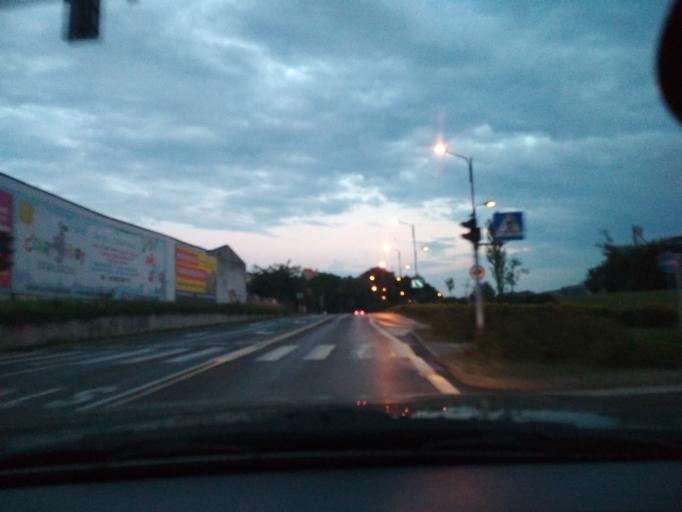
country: PL
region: Silesian Voivodeship
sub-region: Gliwice
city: Gliwice
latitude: 50.2877
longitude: 18.6554
